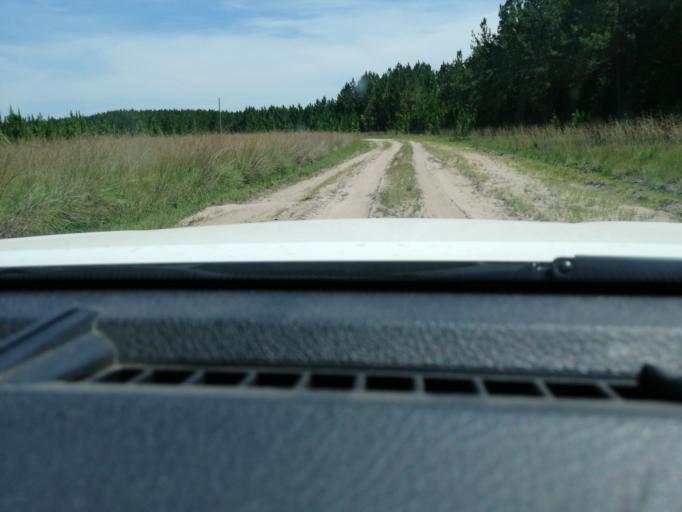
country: AR
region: Corrientes
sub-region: Departamento de San Miguel
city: San Miguel
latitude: -28.0249
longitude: -57.4775
